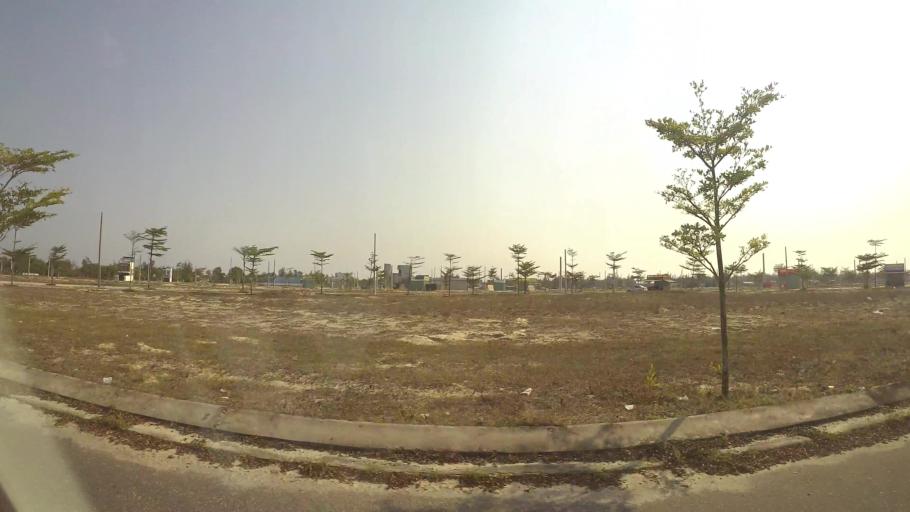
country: VN
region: Da Nang
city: Ngu Hanh Son
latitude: 15.9566
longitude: 108.2756
